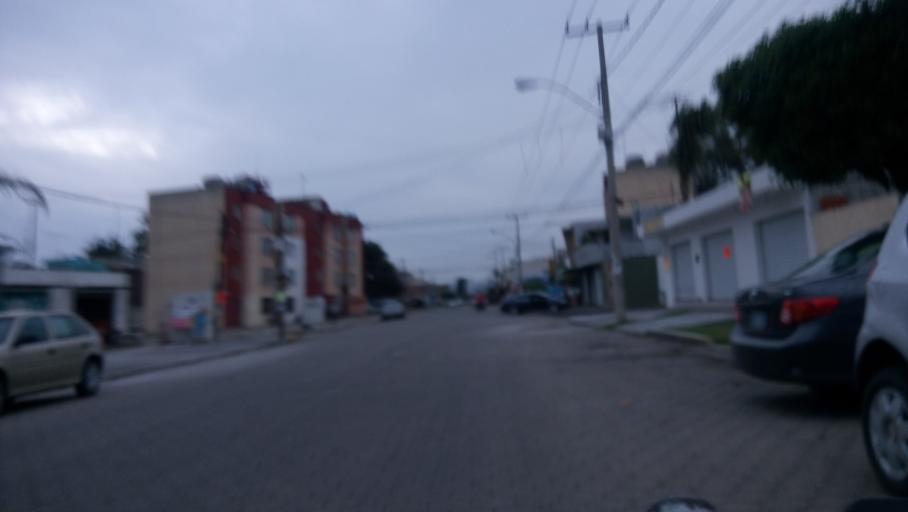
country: MX
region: Guanajuato
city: Leon
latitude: 21.1466
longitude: -101.6637
